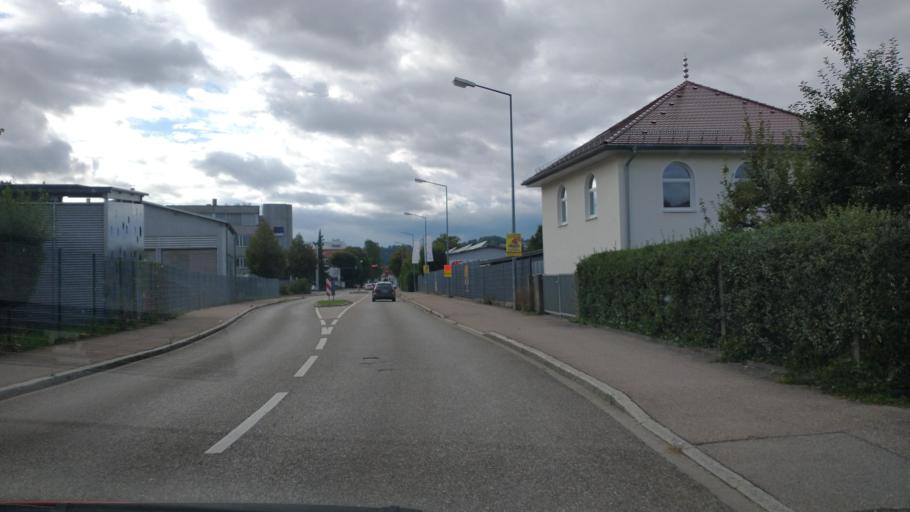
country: DE
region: Baden-Wuerttemberg
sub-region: Regierungsbezirk Stuttgart
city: Schwabisch Gmund
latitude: 48.8015
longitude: 9.8207
